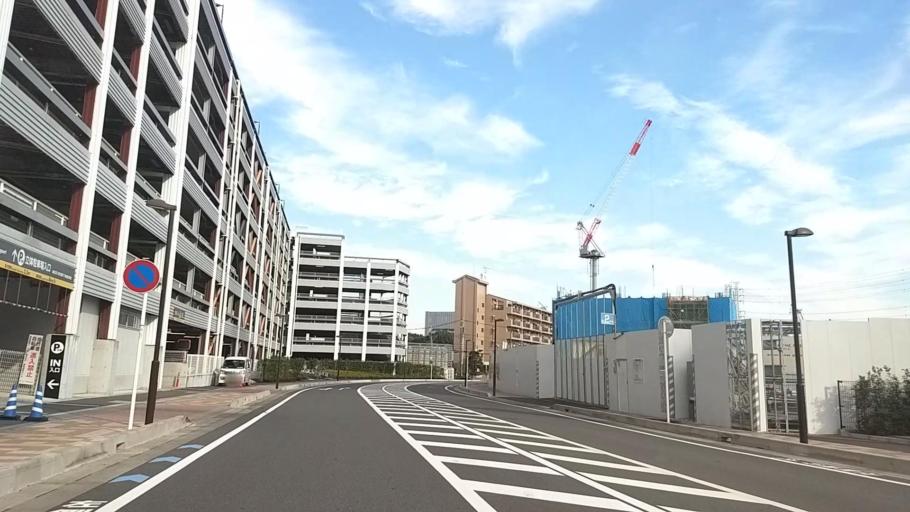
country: JP
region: Kanagawa
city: Zama
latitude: 35.4552
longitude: 139.3898
